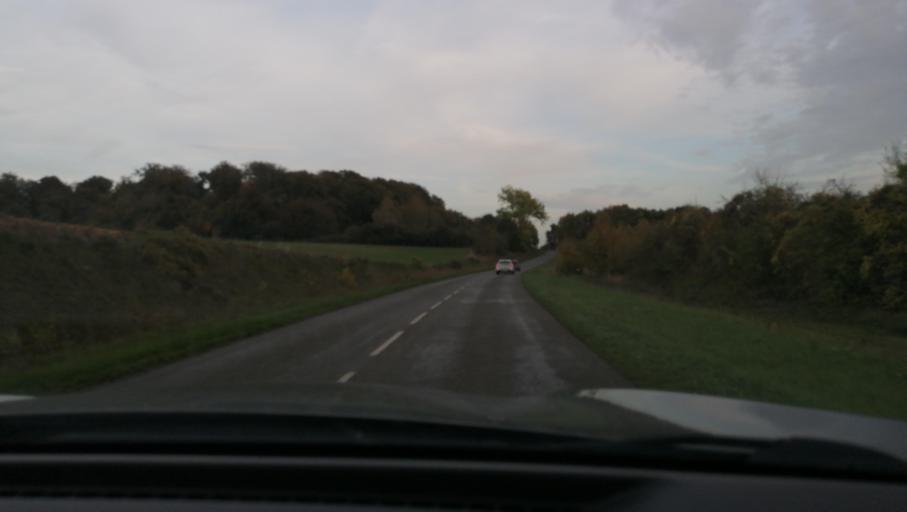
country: FR
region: Picardie
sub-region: Departement de la Somme
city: Ailly-sur-Somme
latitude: 49.8902
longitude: 2.1655
